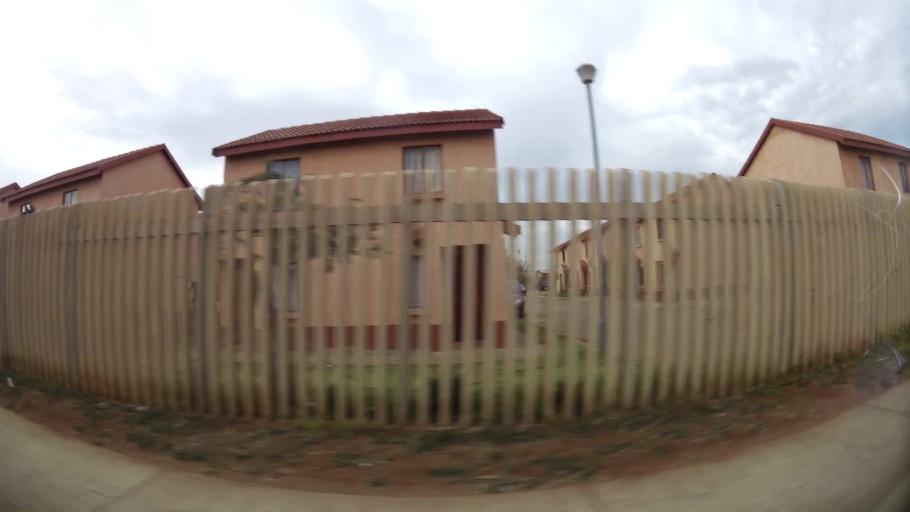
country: ZA
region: Gauteng
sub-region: City of Tshwane Metropolitan Municipality
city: Pretoria
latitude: -25.7077
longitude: 28.3292
